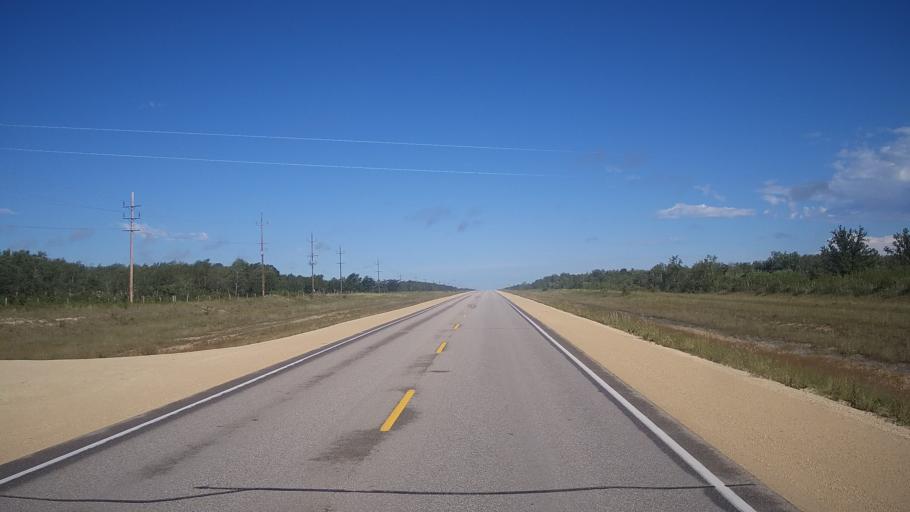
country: CA
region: Manitoba
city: Stonewall
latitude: 50.2170
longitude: -97.6775
